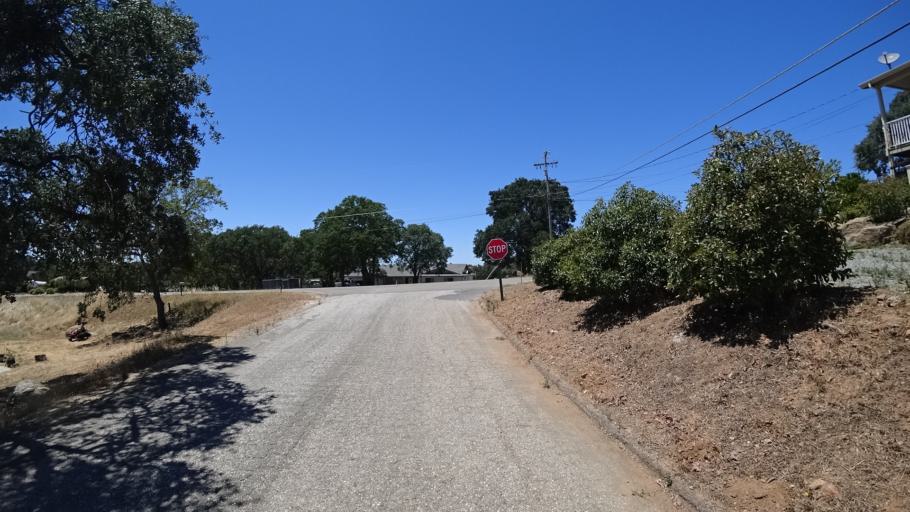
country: US
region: California
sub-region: Calaveras County
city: Valley Springs
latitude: 38.1620
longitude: -120.8381
